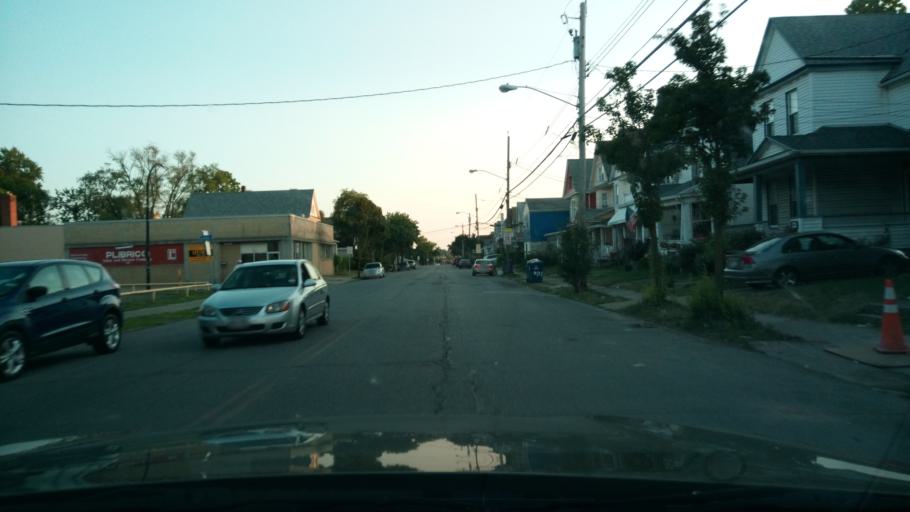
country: US
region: New York
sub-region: Erie County
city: Kenmore
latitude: 42.9491
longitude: -78.9044
